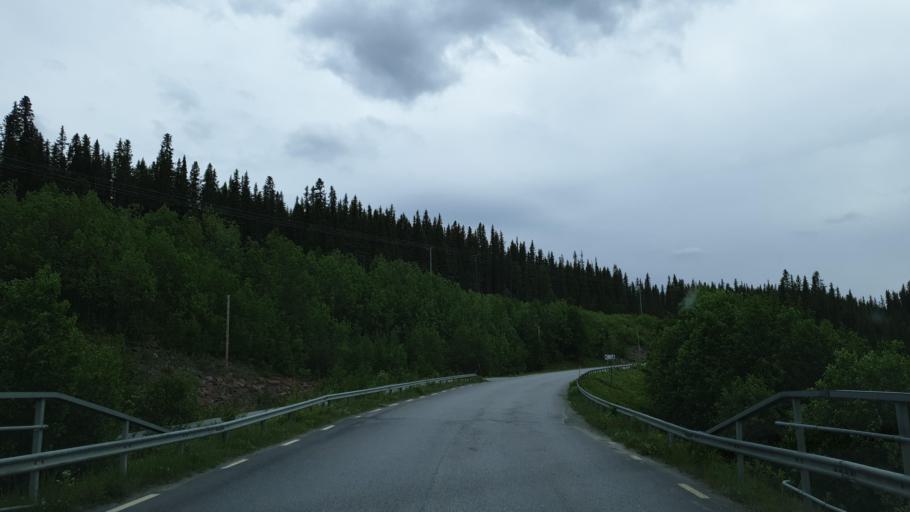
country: SE
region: Vaesterbotten
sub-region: Storumans Kommun
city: Fristad
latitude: 65.4234
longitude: 16.1717
